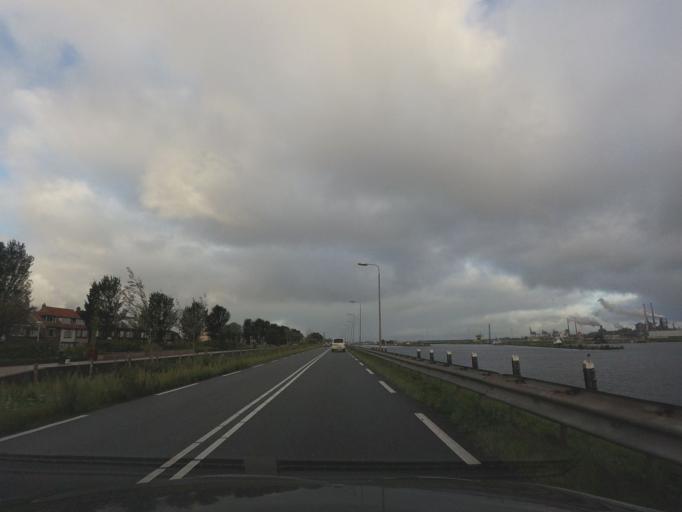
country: NL
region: North Holland
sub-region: Gemeente Velsen
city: Velsen-Zuid
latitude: 52.4635
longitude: 4.6212
